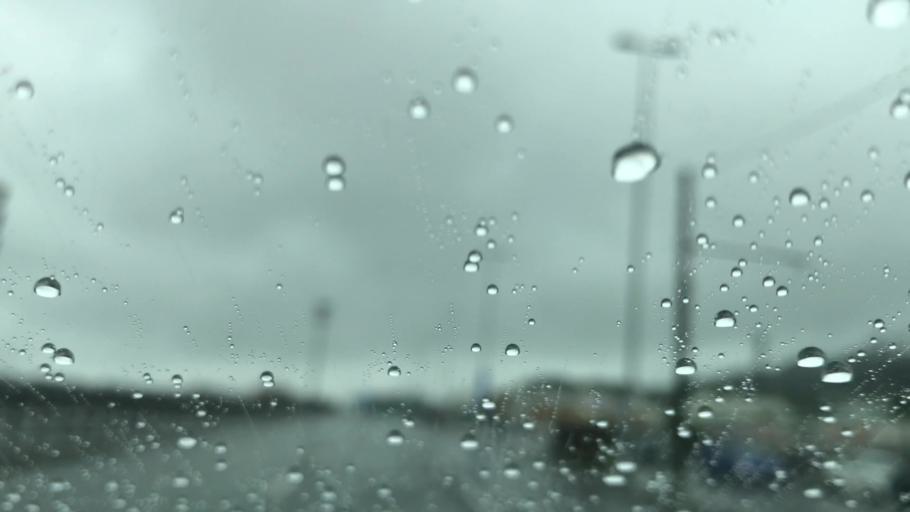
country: JP
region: Hokkaido
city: Otaru
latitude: 43.1850
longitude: 141.0162
